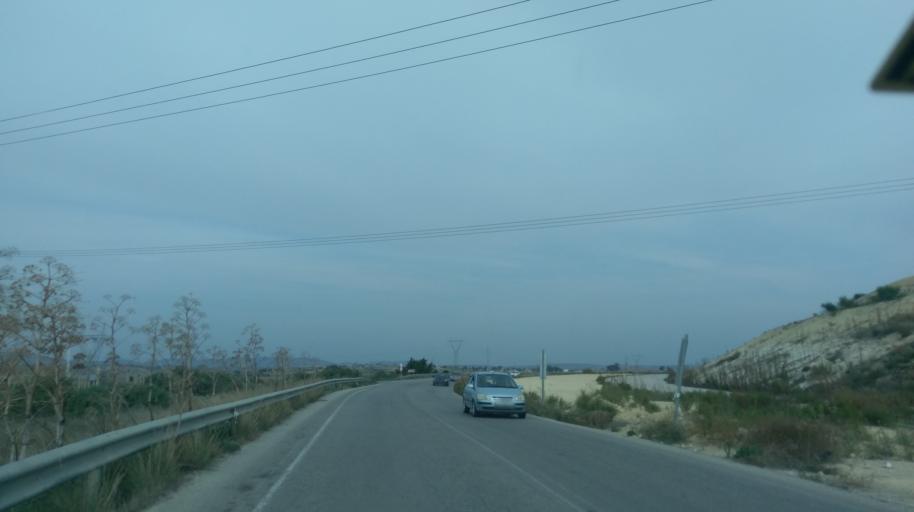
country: CY
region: Ammochostos
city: Trikomo
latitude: 35.3461
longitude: 33.9861
